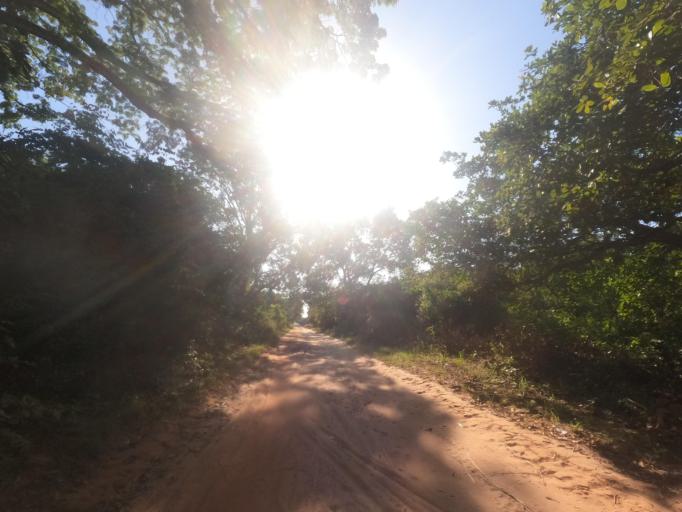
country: GW
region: Cacheu
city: Cacheu
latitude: 12.3944
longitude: -16.2173
